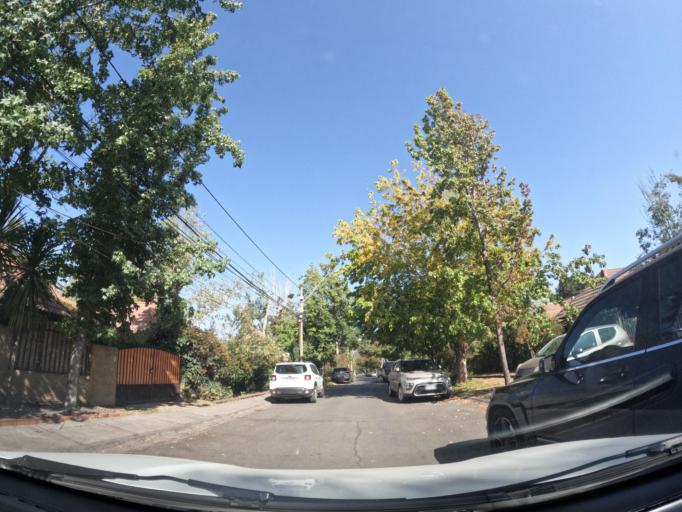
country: CL
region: Santiago Metropolitan
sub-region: Provincia de Santiago
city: Villa Presidente Frei, Nunoa, Santiago, Chile
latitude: -33.5057
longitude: -70.5580
